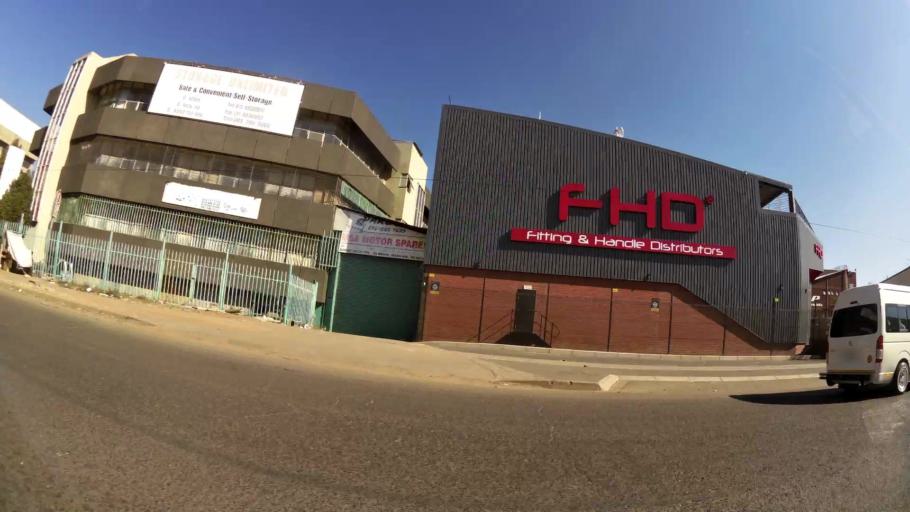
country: ZA
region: Gauteng
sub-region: City of Johannesburg Metropolitan Municipality
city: Johannesburg
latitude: -26.2155
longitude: 28.0488
